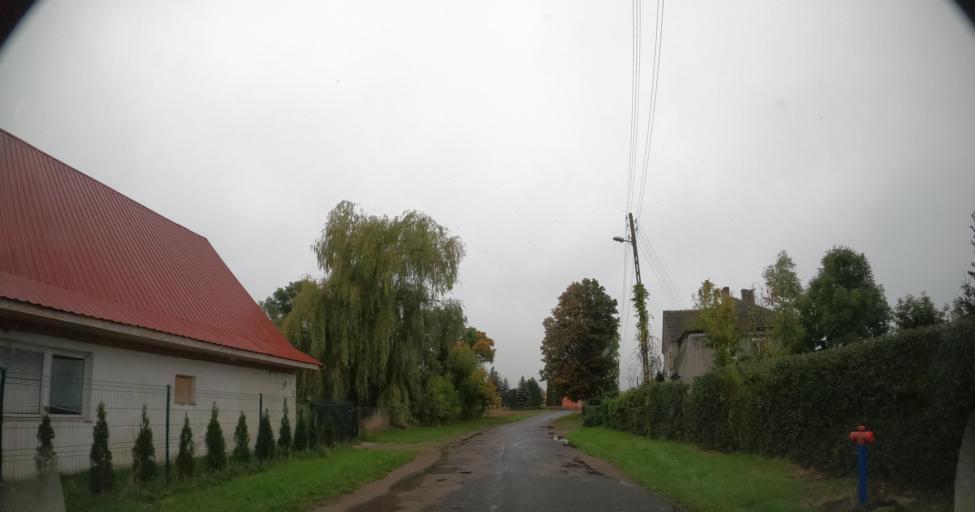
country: PL
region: West Pomeranian Voivodeship
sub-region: Powiat pyrzycki
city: Kozielice
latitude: 53.0470
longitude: 14.7643
